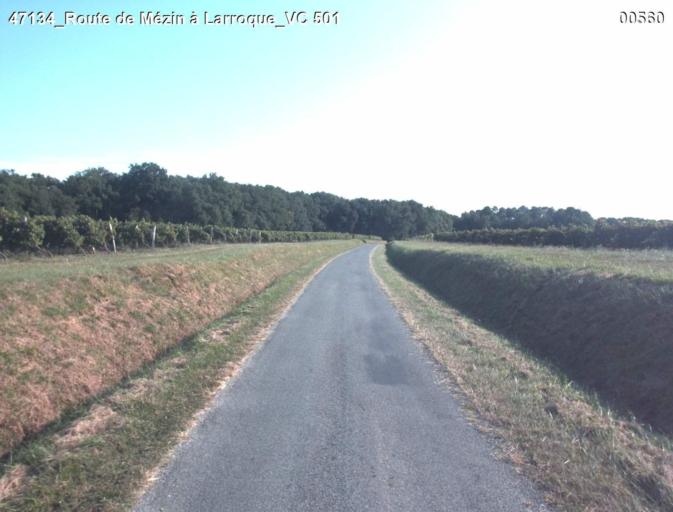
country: FR
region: Aquitaine
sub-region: Departement du Lot-et-Garonne
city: Mezin
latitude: 44.0037
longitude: 0.2784
